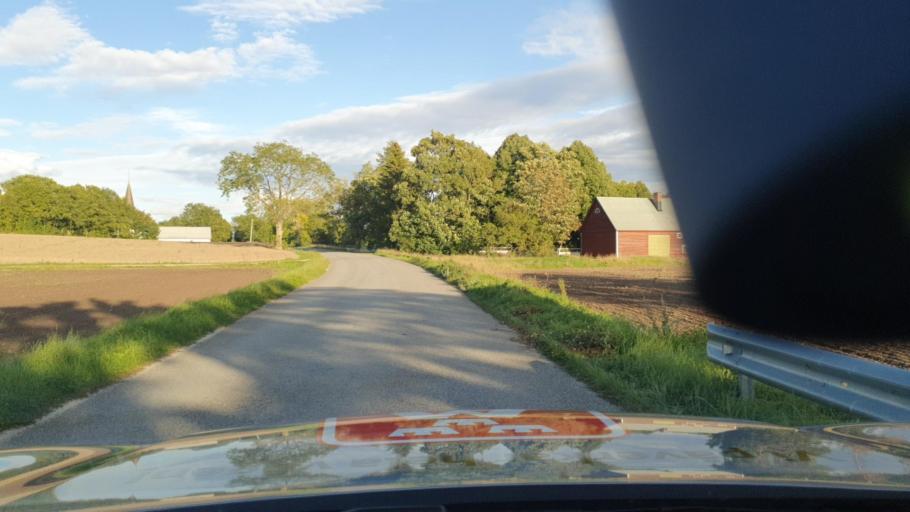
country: SE
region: Gotland
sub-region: Gotland
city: Hemse
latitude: 57.4522
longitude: 18.5054
